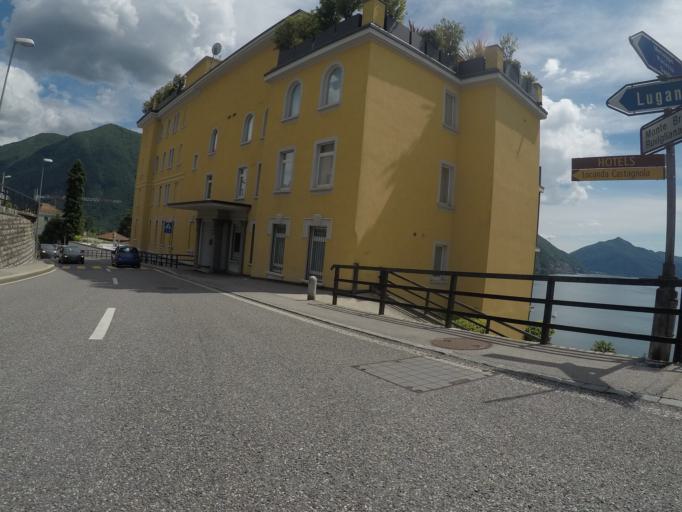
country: CH
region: Ticino
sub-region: Lugano District
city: Viganello
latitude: 46.0017
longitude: 8.9753
